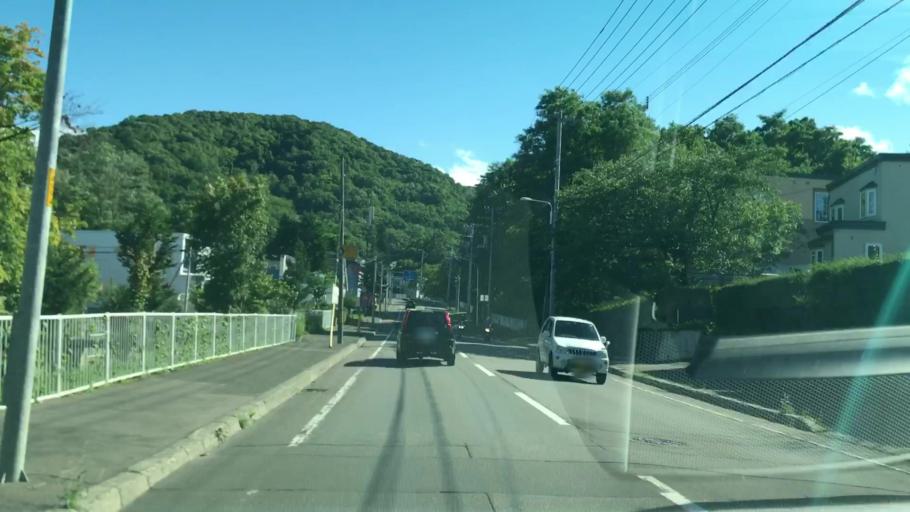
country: JP
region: Hokkaido
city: Sapporo
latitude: 43.0532
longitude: 141.2985
